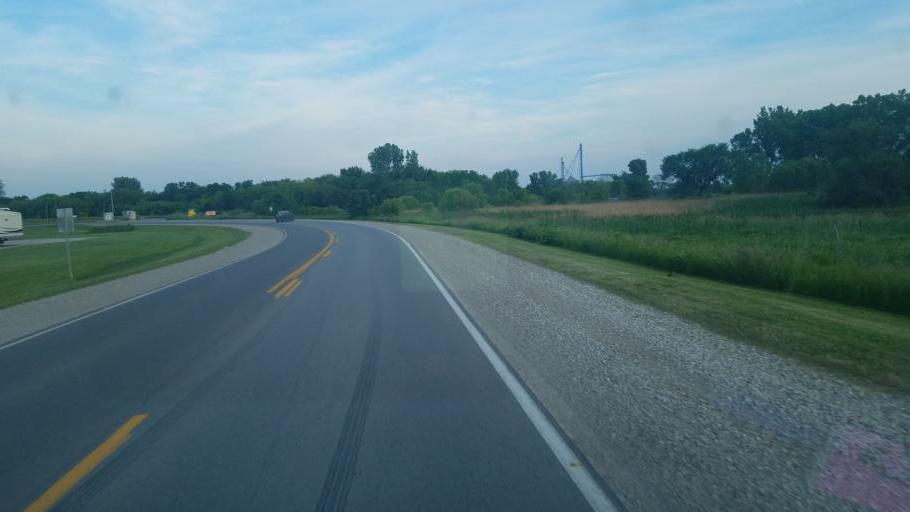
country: US
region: Iowa
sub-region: Benton County
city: Belle Plaine
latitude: 41.8989
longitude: -92.2907
